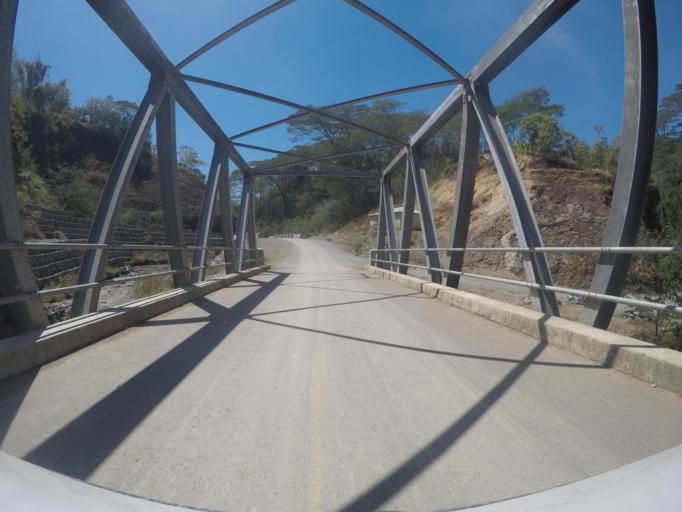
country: TL
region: Ermera
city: Gleno
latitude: -8.7896
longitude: 125.3782
